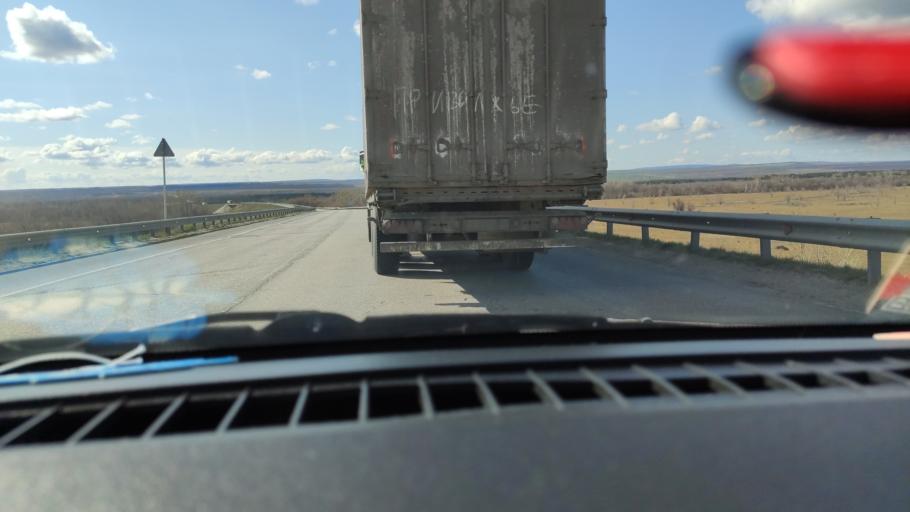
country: RU
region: Samara
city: Varlamovo
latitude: 53.1700
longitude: 48.2809
